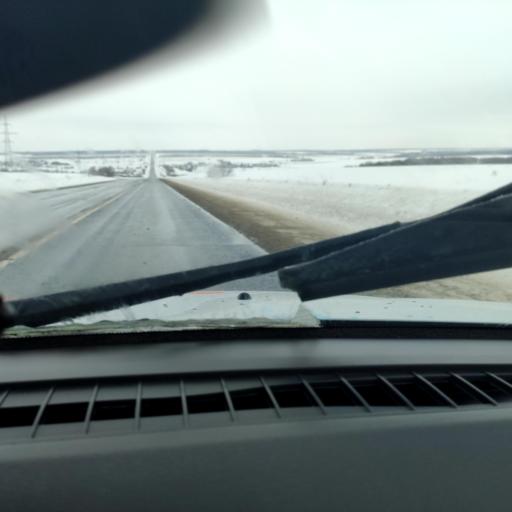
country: RU
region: Samara
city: Novokuybyshevsk
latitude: 53.0100
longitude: 50.0449
